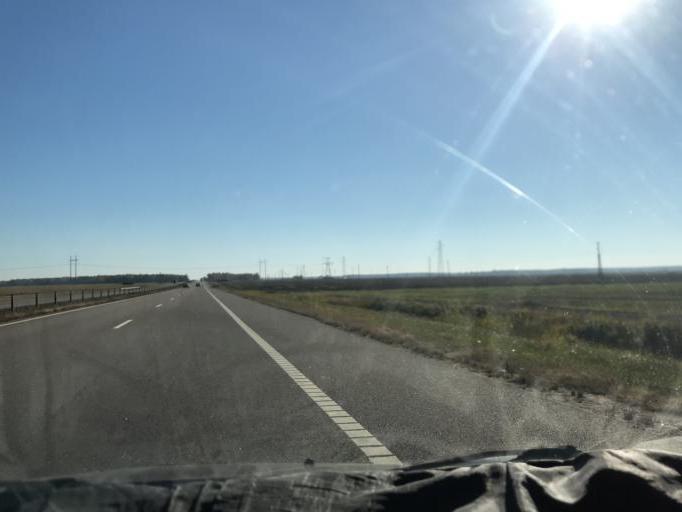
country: BY
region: Mogilev
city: Yalizava
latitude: 53.2313
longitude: 28.9865
